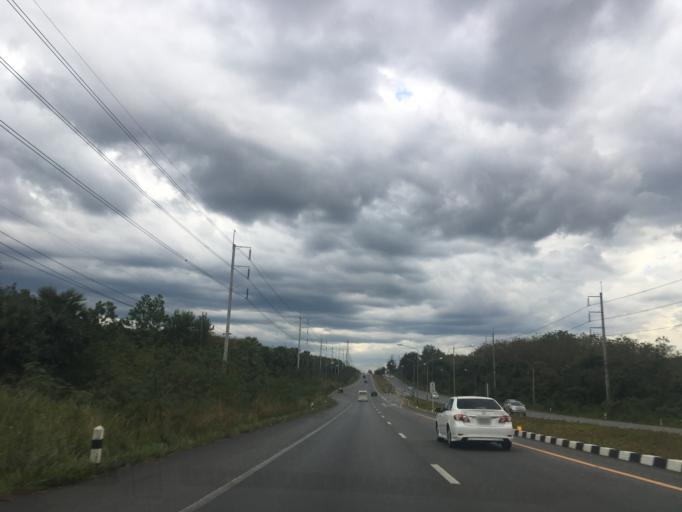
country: TH
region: Chon Buri
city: Nong Yai
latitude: 13.1778
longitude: 101.2667
